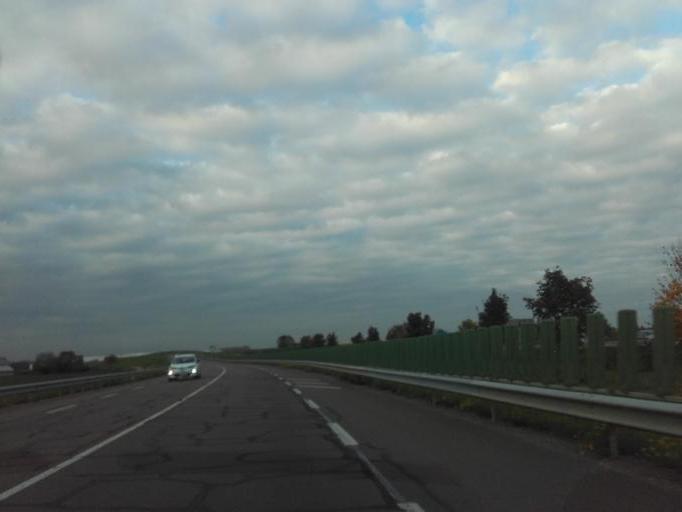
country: FR
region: Bourgogne
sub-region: Departement de Saone-et-Loire
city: Champforgeuil
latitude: 46.8222
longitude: 4.8293
